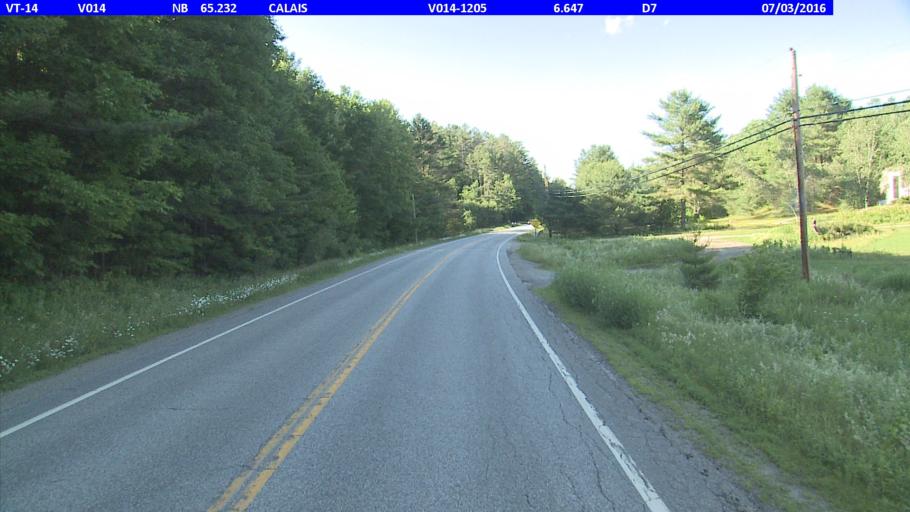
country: US
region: Vermont
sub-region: Caledonia County
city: Hardwick
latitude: 44.3926
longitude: -72.4148
